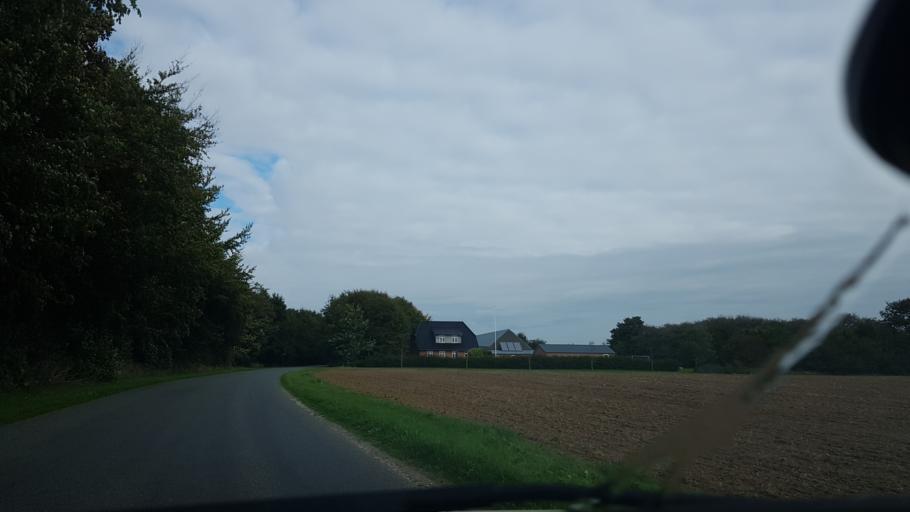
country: DK
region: South Denmark
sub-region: Vejen Kommune
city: Brorup
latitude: 55.4681
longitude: 8.9690
